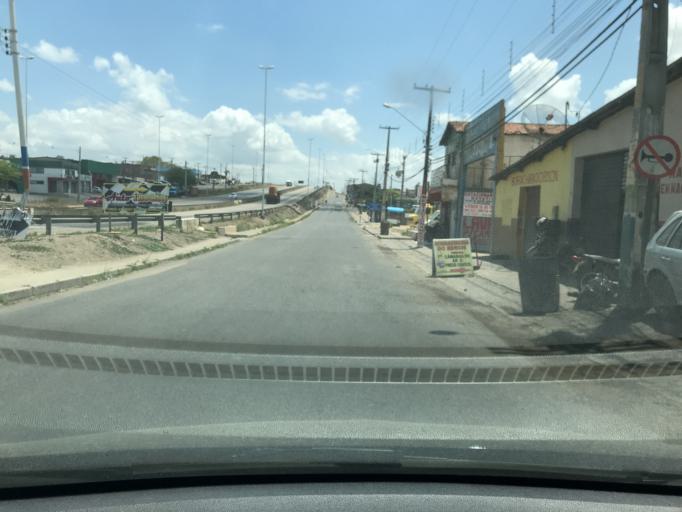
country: BR
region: Pernambuco
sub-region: Bezerros
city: Bezerros
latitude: -8.2448
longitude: -35.7553
